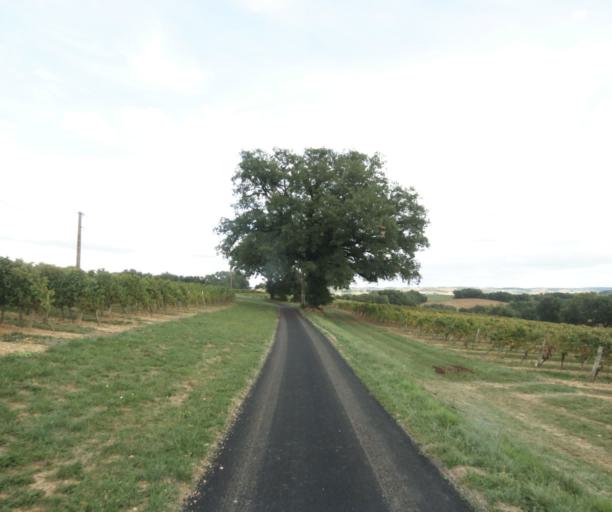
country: FR
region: Midi-Pyrenees
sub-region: Departement du Gers
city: Gondrin
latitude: 43.8699
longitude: 0.2546
